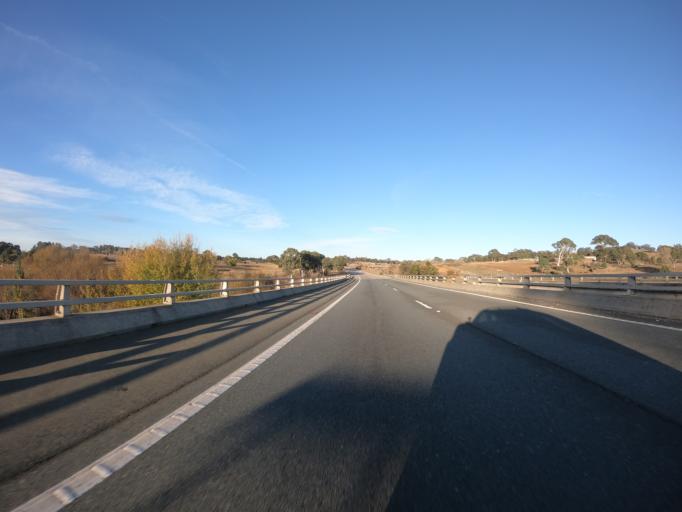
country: AU
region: New South Wales
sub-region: Yass Valley
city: Gundaroo
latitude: -35.1194
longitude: 149.3483
